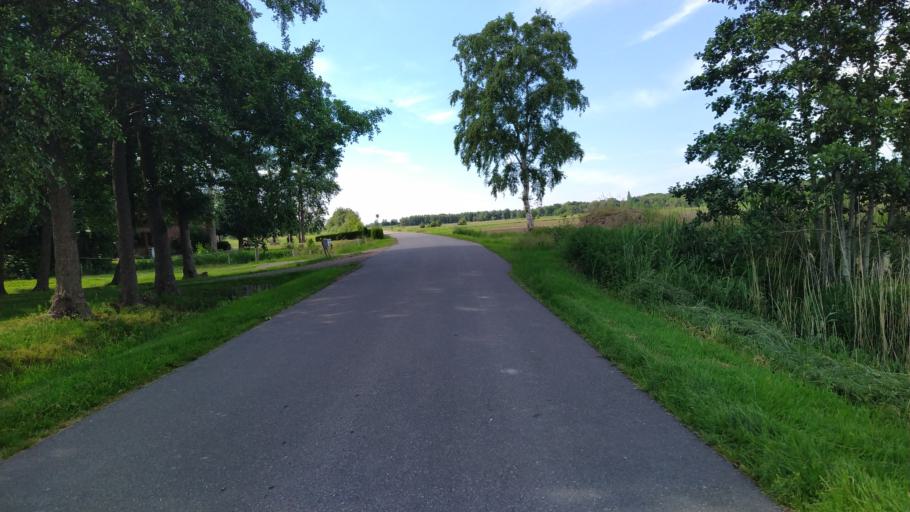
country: DE
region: Lower Saxony
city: Odisheim
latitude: 53.6647
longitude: 8.9289
